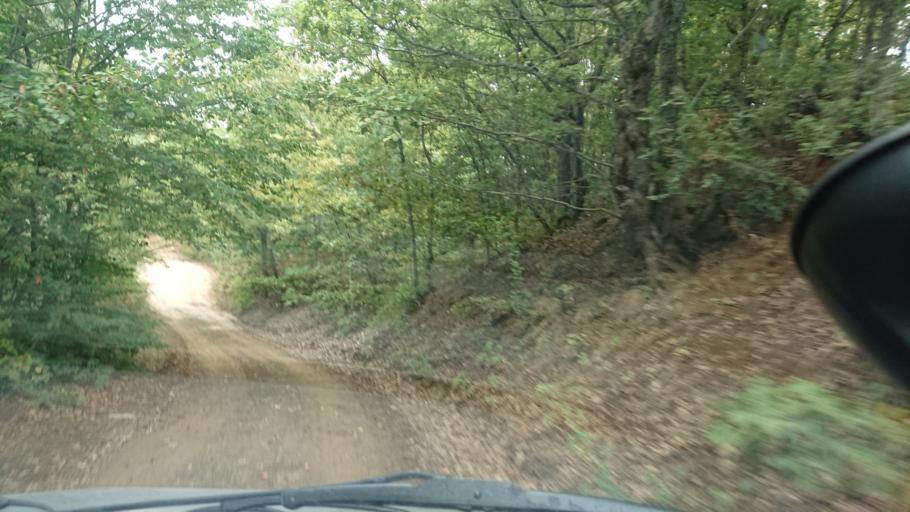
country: TR
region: Bilecik
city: Pazaryeri
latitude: 40.0187
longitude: 29.7901
